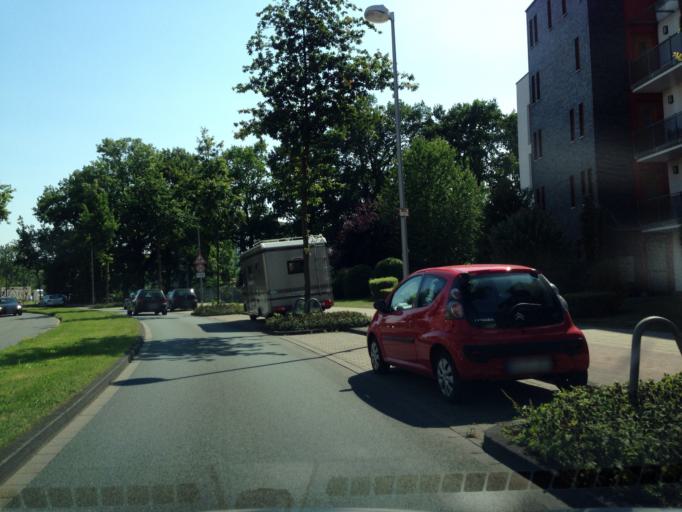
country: DE
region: North Rhine-Westphalia
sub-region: Regierungsbezirk Munster
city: Muenster
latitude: 51.9691
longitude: 7.5622
